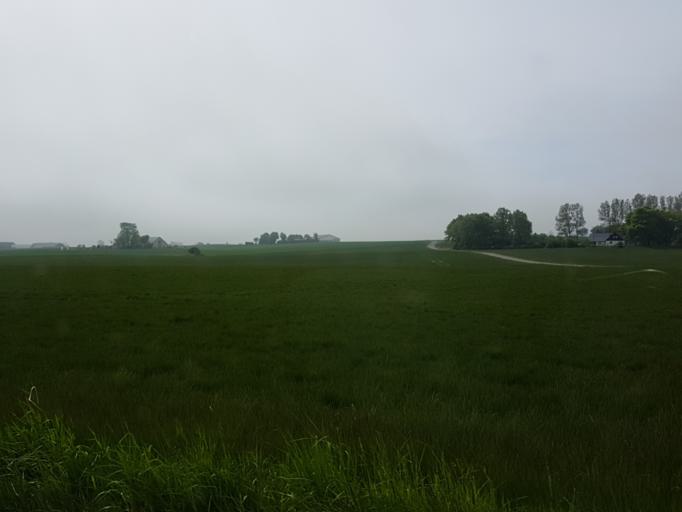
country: SE
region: Skane
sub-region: Tomelilla Kommun
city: Tomelilla
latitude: 55.5071
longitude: 14.0274
